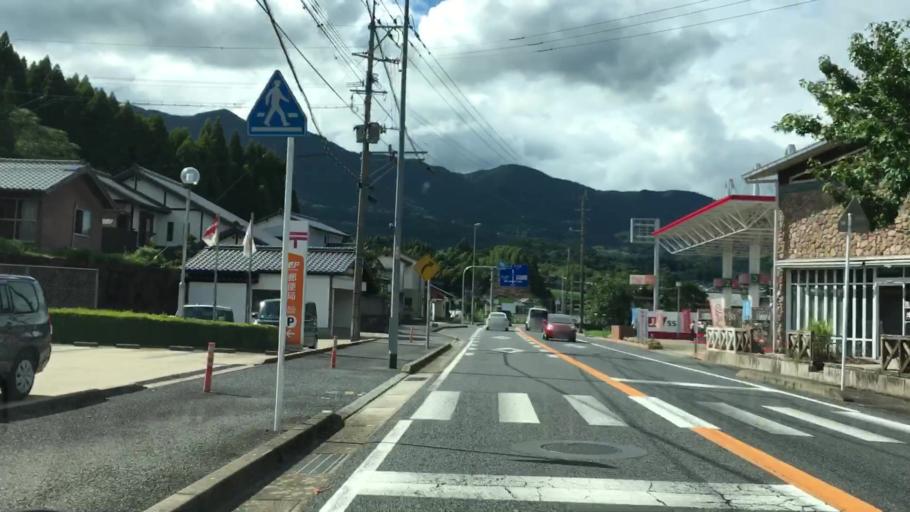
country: JP
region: Saga Prefecture
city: Imaricho-ko
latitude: 33.2225
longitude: 129.8489
